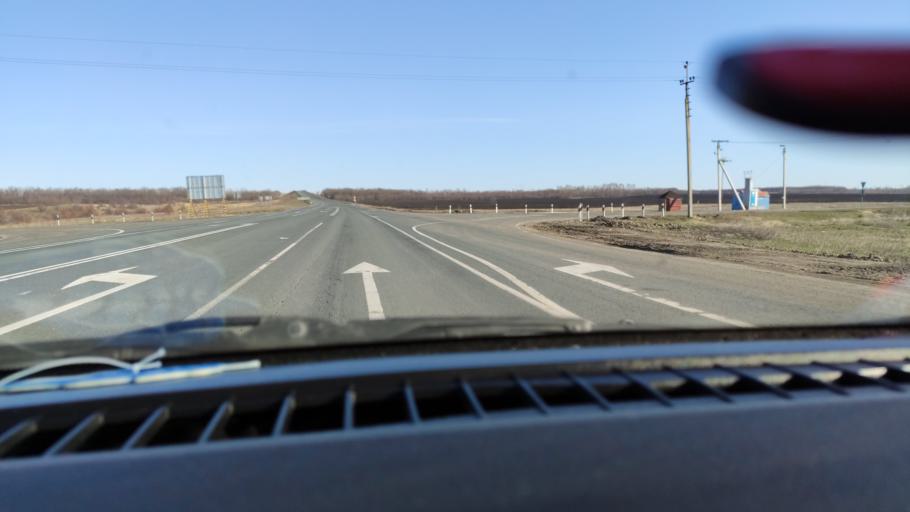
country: RU
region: Saratov
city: Dukhovnitskoye
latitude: 52.7443
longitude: 48.2527
